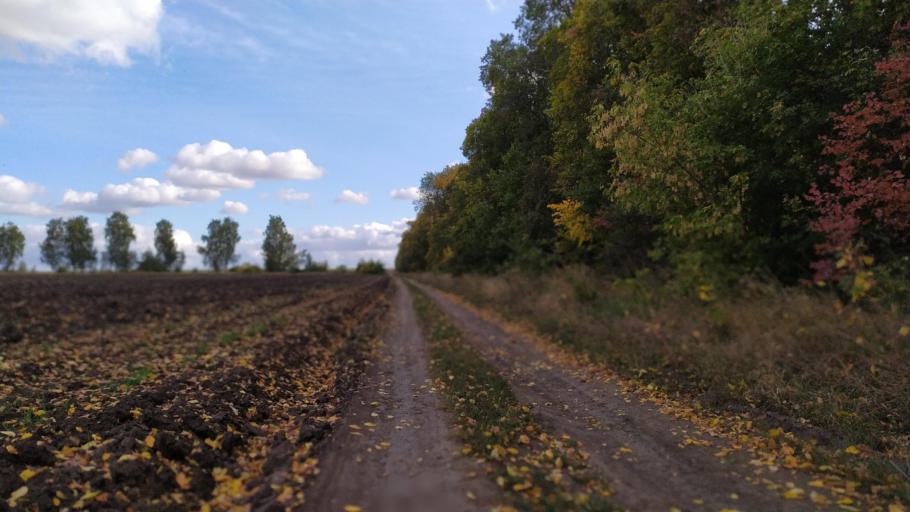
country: RU
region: Kursk
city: Kursk
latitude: 51.6240
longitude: 36.1610
